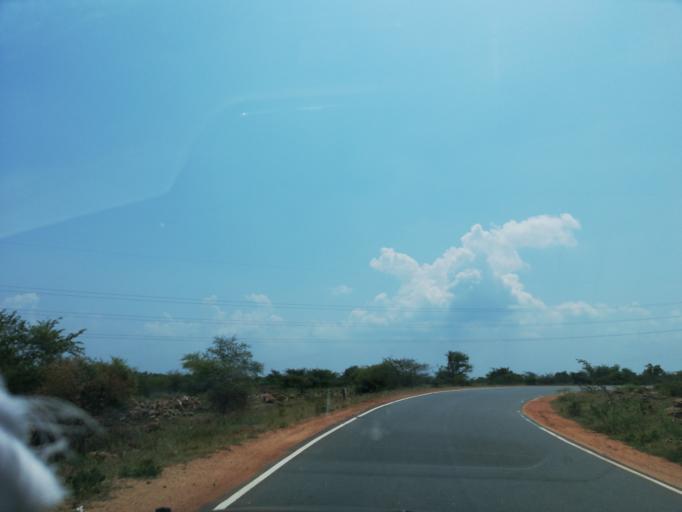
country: IN
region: Andhra Pradesh
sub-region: Guntur
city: Macherla
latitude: 16.5677
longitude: 79.3468
